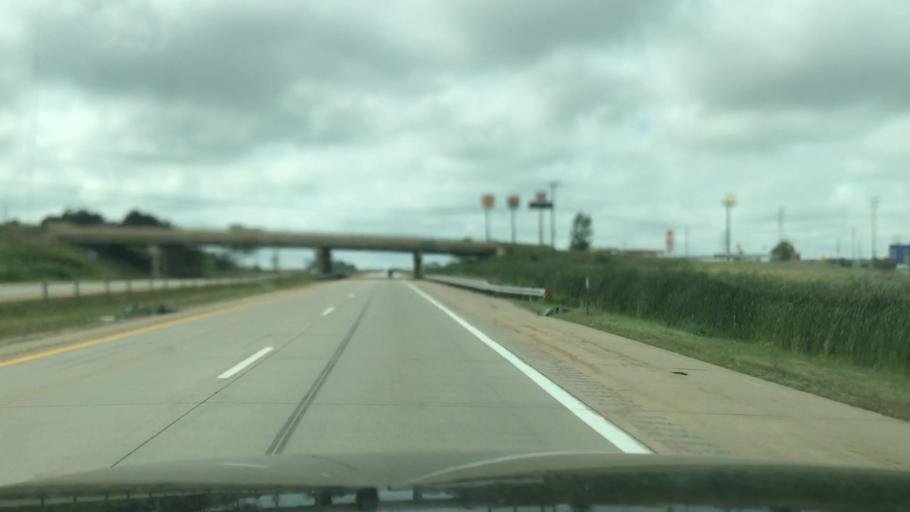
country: US
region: Michigan
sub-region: Ottawa County
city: Coopersville
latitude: 43.0557
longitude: -85.9554
